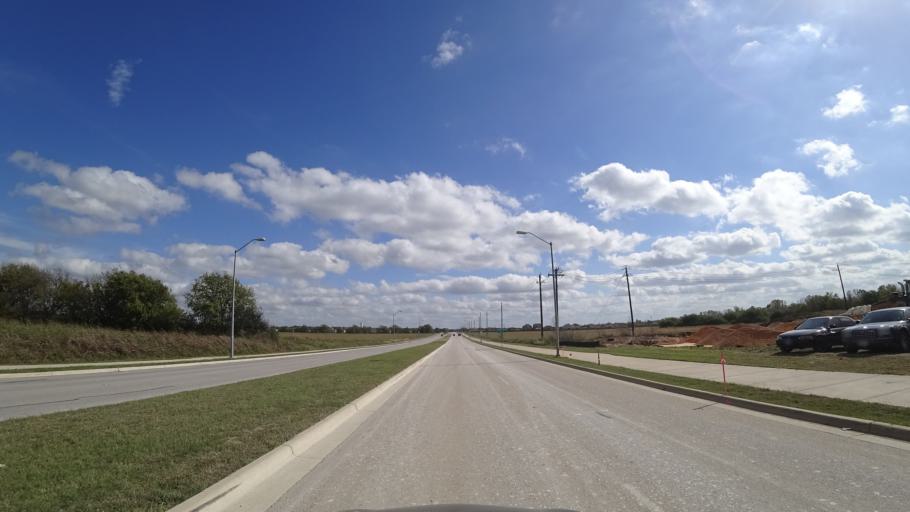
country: US
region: Texas
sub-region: Travis County
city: Windemere
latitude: 30.4763
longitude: -97.6617
